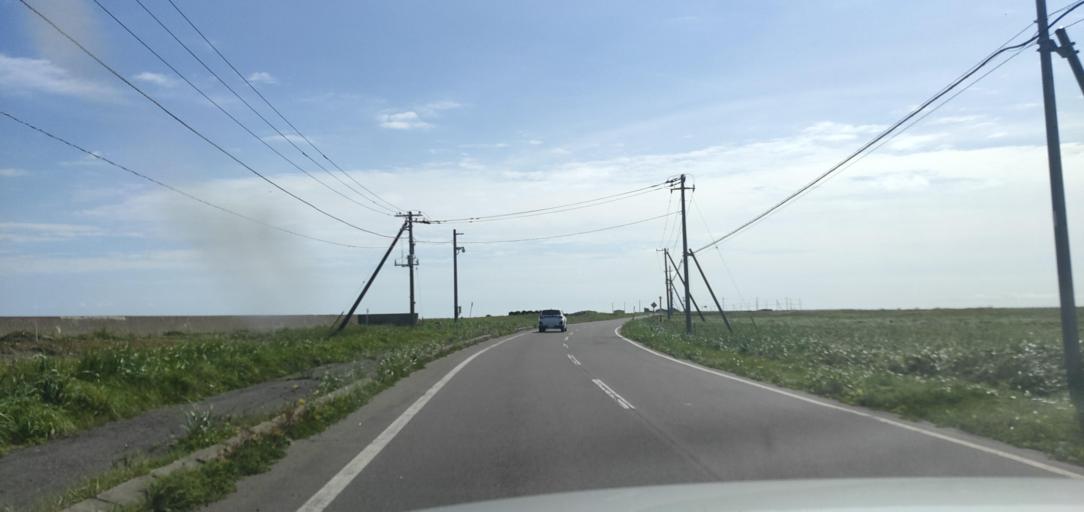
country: JP
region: Hokkaido
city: Shibetsu
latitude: 43.6276
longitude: 145.1997
